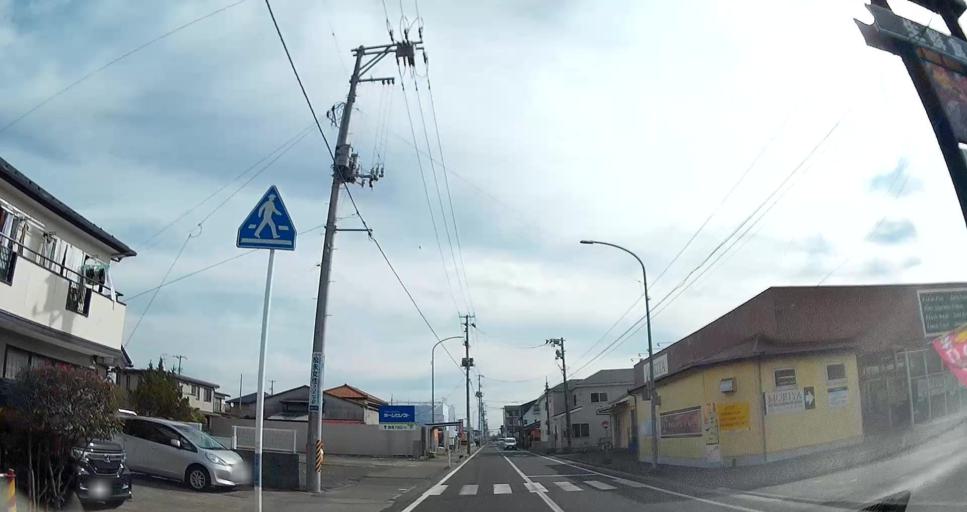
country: JP
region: Miyagi
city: Sendai
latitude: 38.2203
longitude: 140.9143
